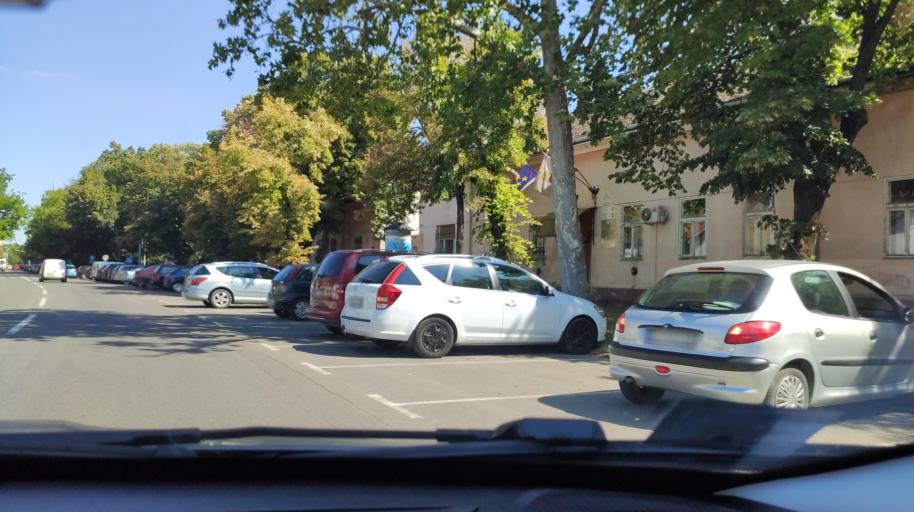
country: RS
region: Autonomna Pokrajina Vojvodina
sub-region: Severnobacki Okrug
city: Backa Topola
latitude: 45.8101
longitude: 19.6308
